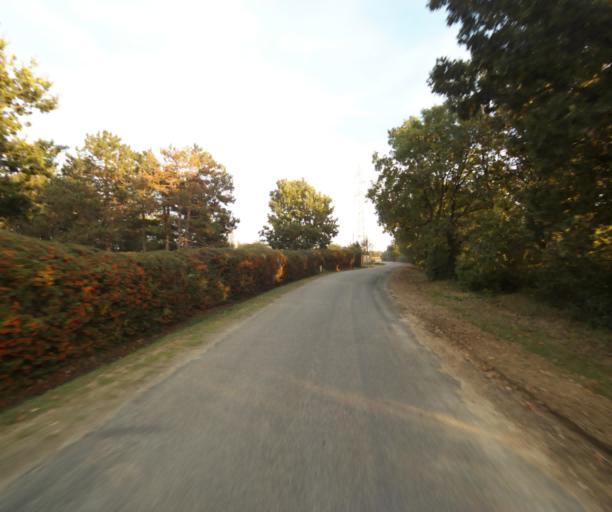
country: FR
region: Midi-Pyrenees
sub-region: Departement du Tarn-et-Garonne
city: Grisolles
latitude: 43.8316
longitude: 1.3097
